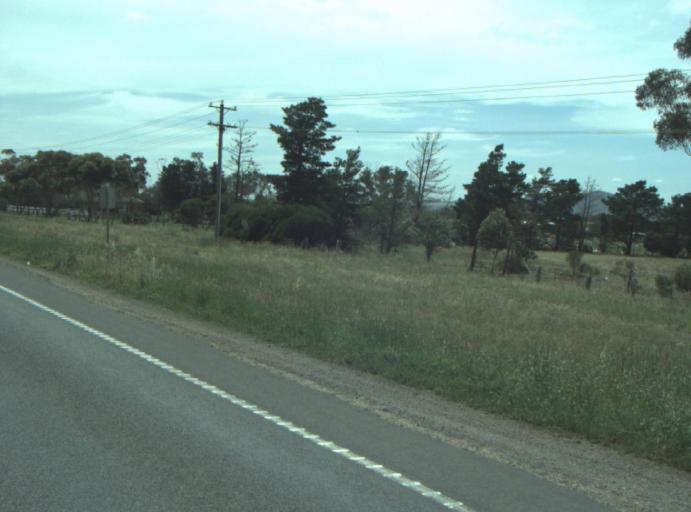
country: AU
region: Victoria
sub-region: Greater Geelong
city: Lara
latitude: -38.0282
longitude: 144.3541
